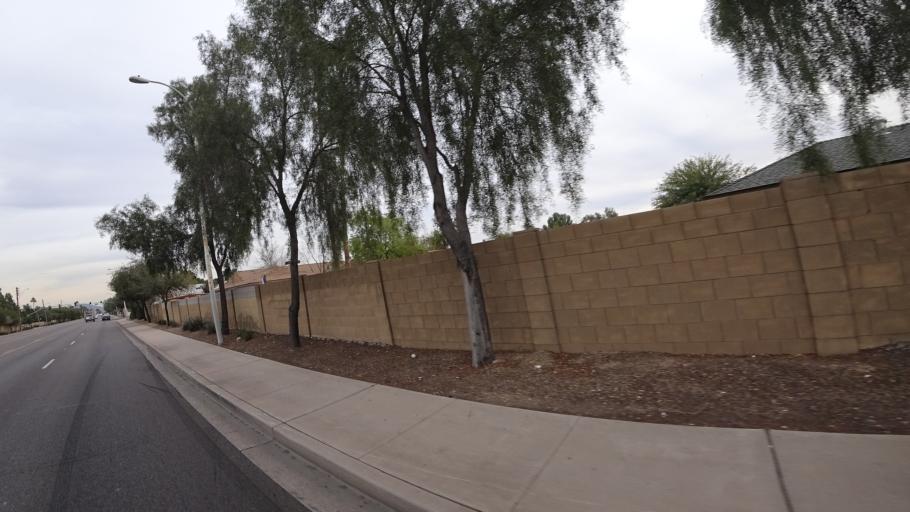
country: US
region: Arizona
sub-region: Maricopa County
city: Glendale
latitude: 33.5819
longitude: -112.1620
